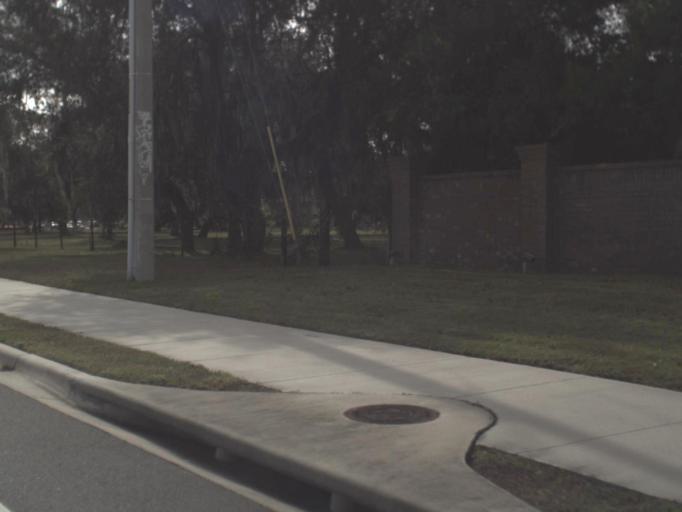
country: US
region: Florida
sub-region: Osceola County
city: Saint Cloud
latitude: 28.3311
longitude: -81.2292
